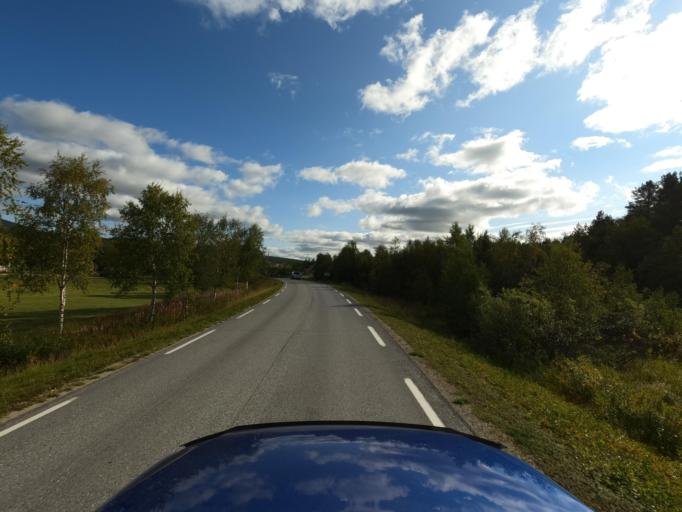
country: NO
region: Finnmark Fylke
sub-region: Karasjok
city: Karasjohka
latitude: 69.4018
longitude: 25.8137
